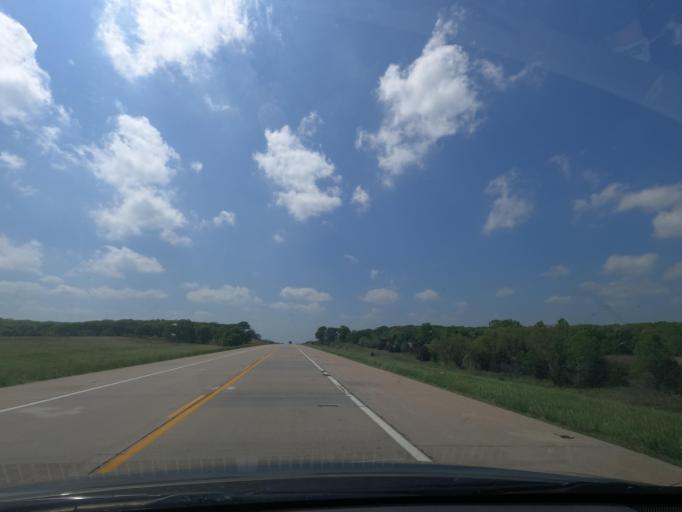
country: US
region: Kansas
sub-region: Wilson County
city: Fredonia
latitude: 37.6169
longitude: -95.9524
